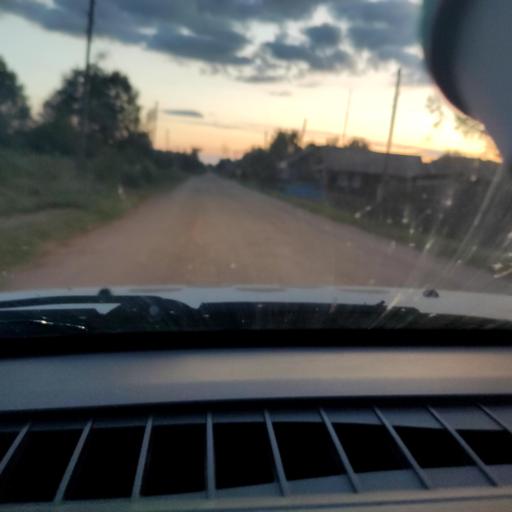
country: RU
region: Kirov
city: Darovskoy
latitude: 58.9893
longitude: 47.8717
